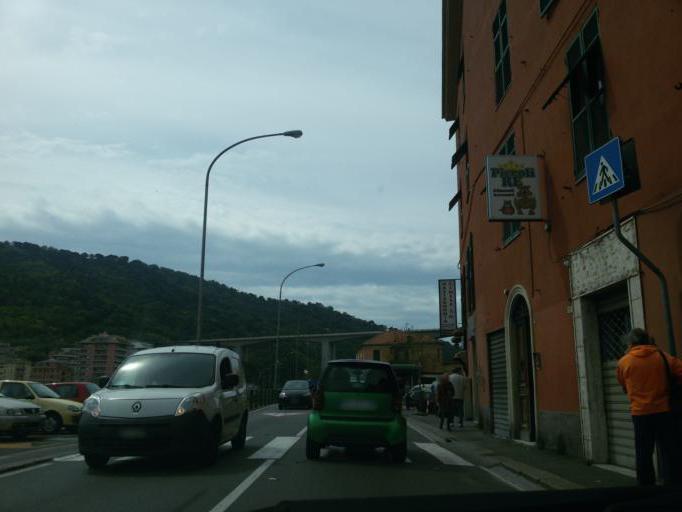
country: IT
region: Liguria
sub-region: Provincia di Genova
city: Piccarello
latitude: 44.4384
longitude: 8.9623
